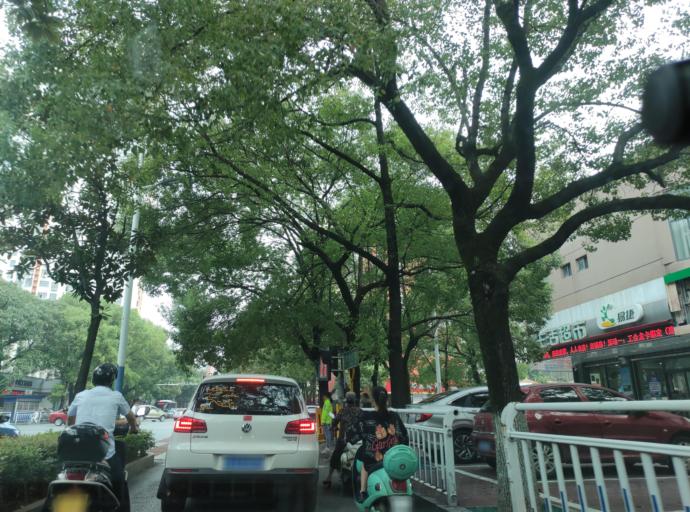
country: CN
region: Jiangxi Sheng
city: Pingxiang
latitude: 27.6437
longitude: 113.8401
